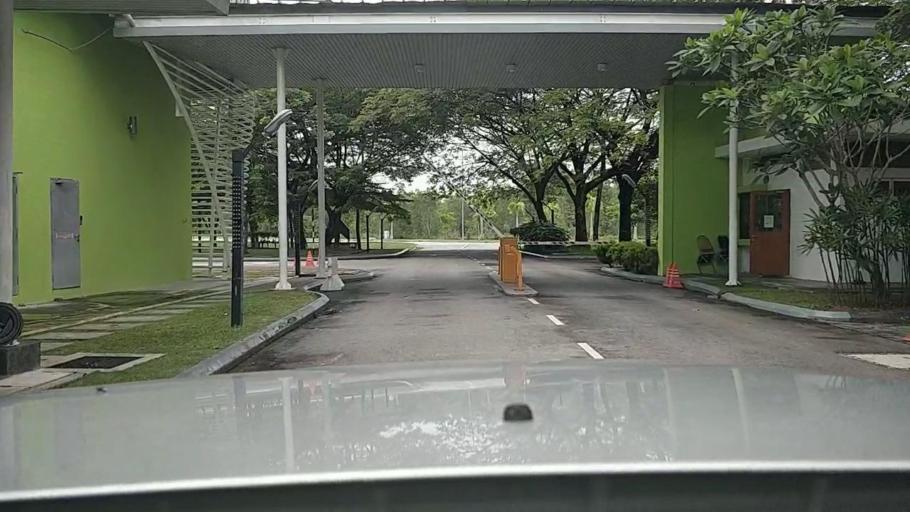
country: MY
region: Putrajaya
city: Putrajaya
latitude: 2.9015
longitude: 101.6522
